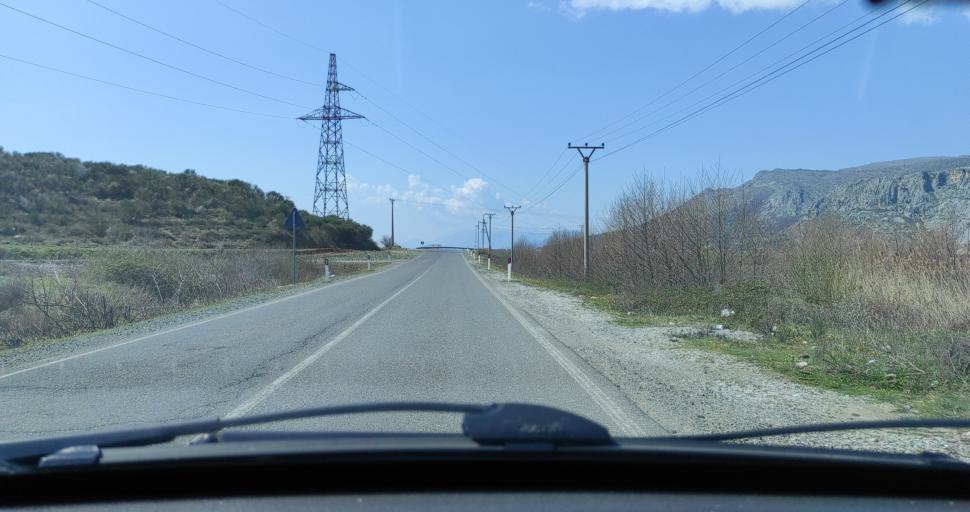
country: AL
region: Shkoder
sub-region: Rrethi i Shkodres
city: Vau i Dejes
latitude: 42.0021
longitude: 19.6291
